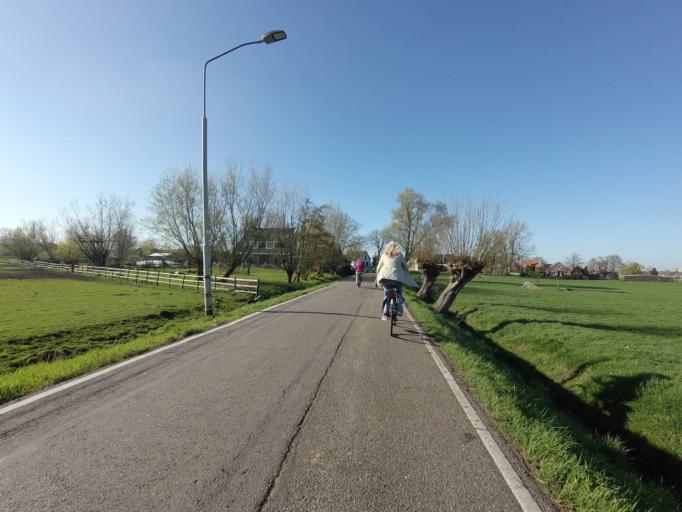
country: NL
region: North Holland
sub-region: Gemeente Heemstede
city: Heemstede
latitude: 52.3409
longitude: 4.6430
